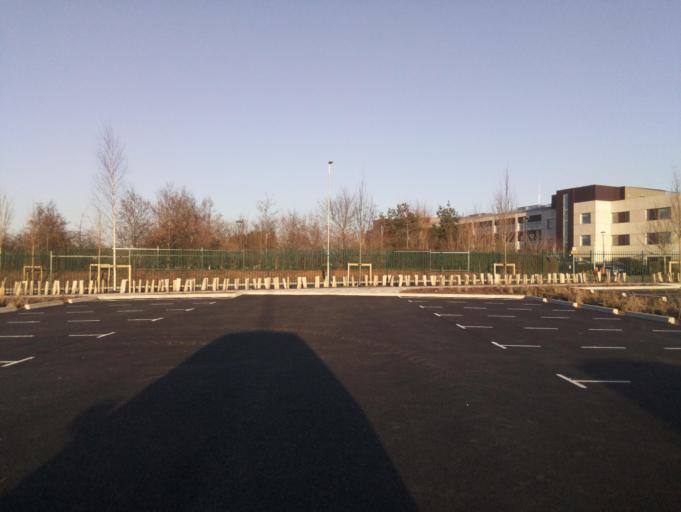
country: GB
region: England
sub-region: South Gloucestershire
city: Yate
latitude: 51.5409
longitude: -2.4410
